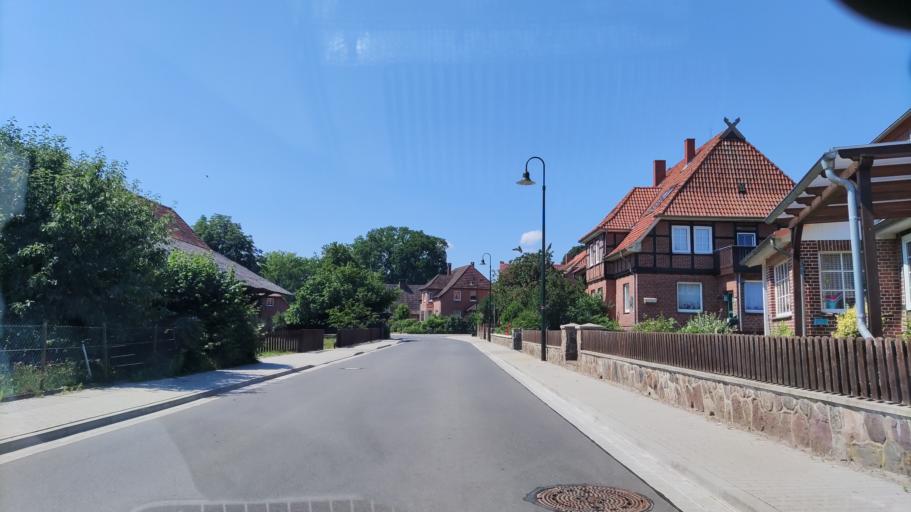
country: DE
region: Lower Saxony
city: Suderburg
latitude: 52.8779
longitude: 10.4086
